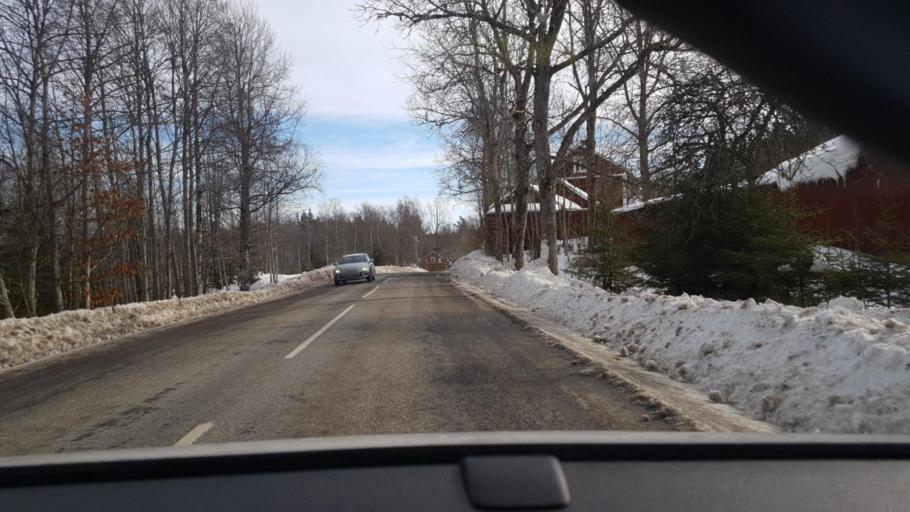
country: SE
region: Vaermland
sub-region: Arjangs Kommun
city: Arjaeng
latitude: 59.5775
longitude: 12.2337
